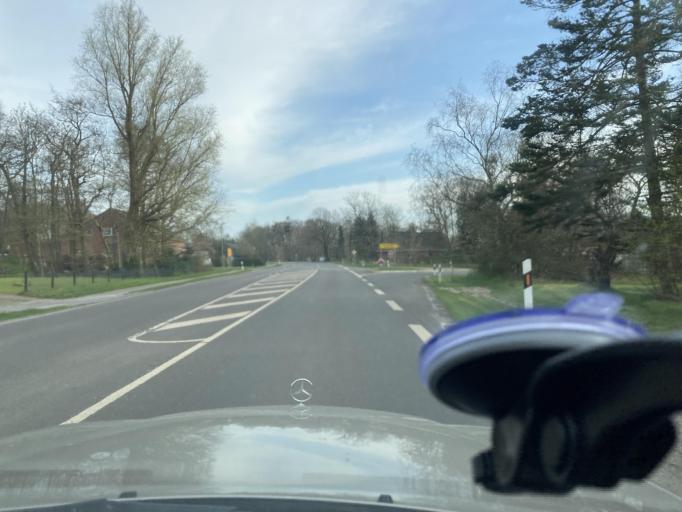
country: DE
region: Schleswig-Holstein
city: Stelle-Wittenwurth
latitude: 54.2720
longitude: 9.0475
